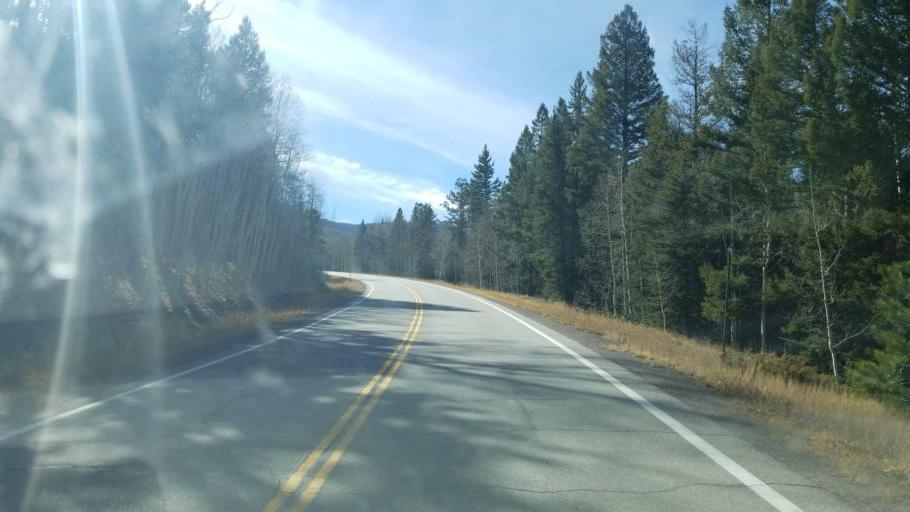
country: US
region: New Mexico
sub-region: Rio Arriba County
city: Chama
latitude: 37.1197
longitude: -106.3680
